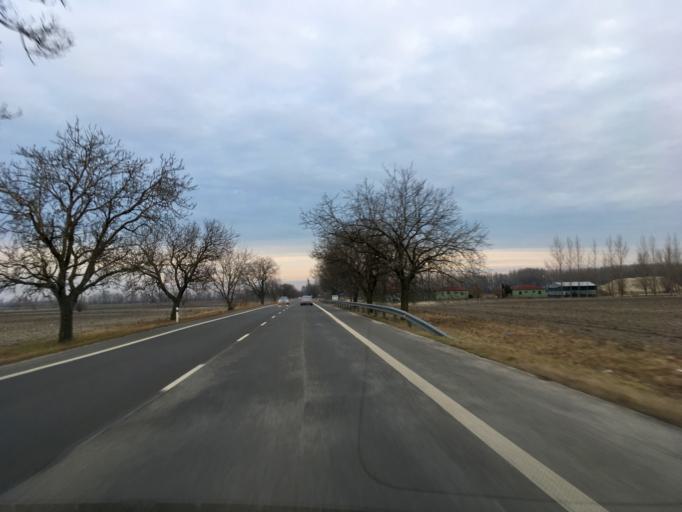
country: SK
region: Trnavsky
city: Dunajska Streda
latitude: 47.9548
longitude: 17.7026
